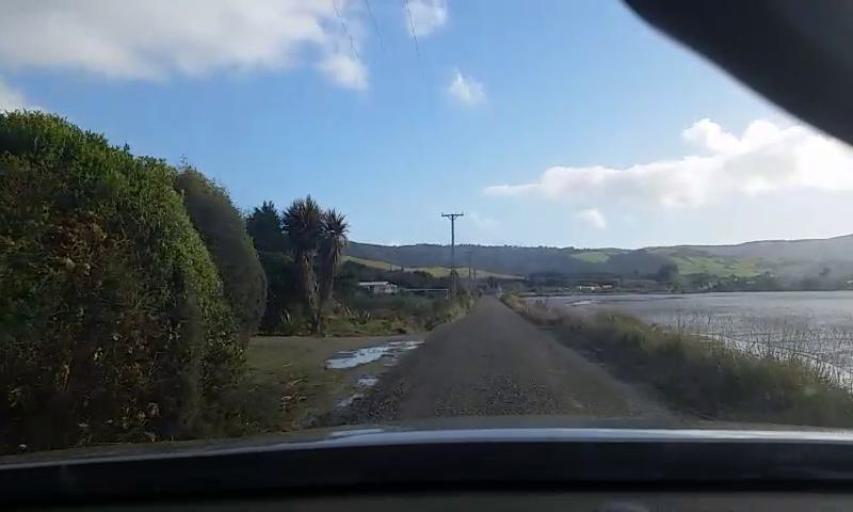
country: NZ
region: Otago
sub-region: Clutha District
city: Papatowai
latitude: -46.6298
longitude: 169.1403
